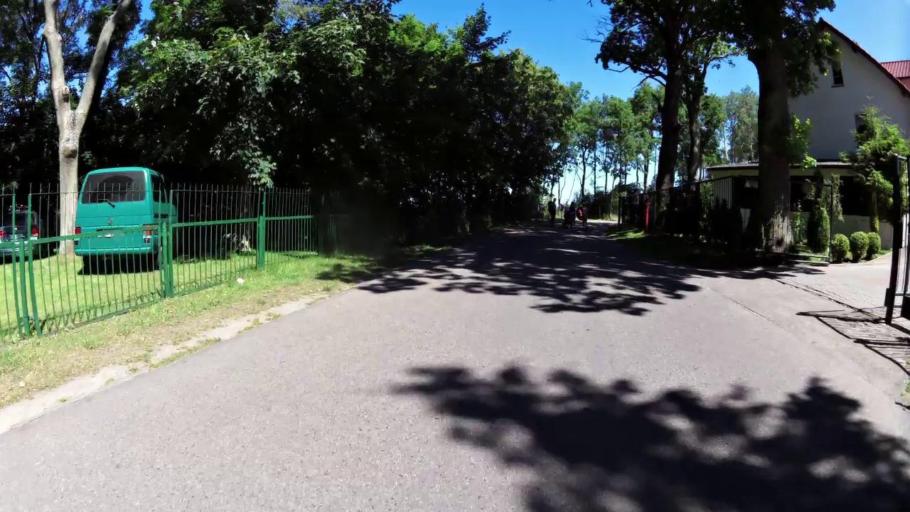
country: PL
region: West Pomeranian Voivodeship
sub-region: Powiat gryficki
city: Rewal
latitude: 54.0872
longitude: 15.0314
